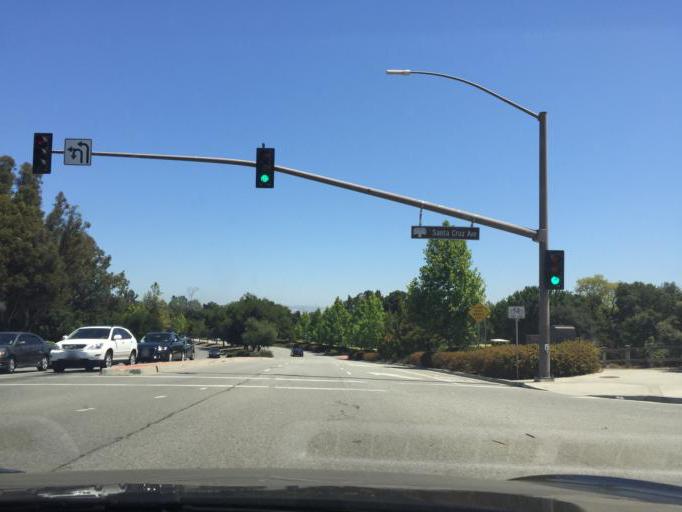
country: US
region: California
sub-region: San Mateo County
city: West Menlo Park
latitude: 37.4258
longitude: -122.1923
